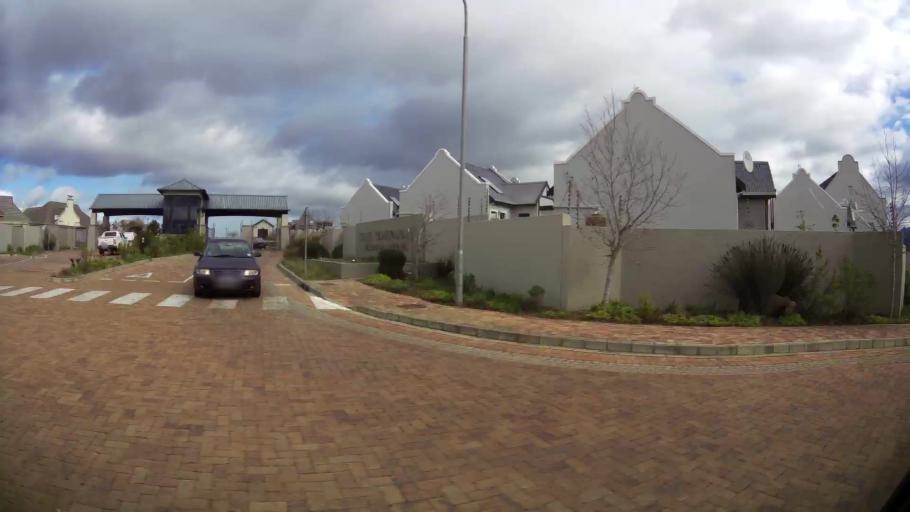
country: ZA
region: Western Cape
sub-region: Eden District Municipality
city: George
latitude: -33.9833
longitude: 22.4971
